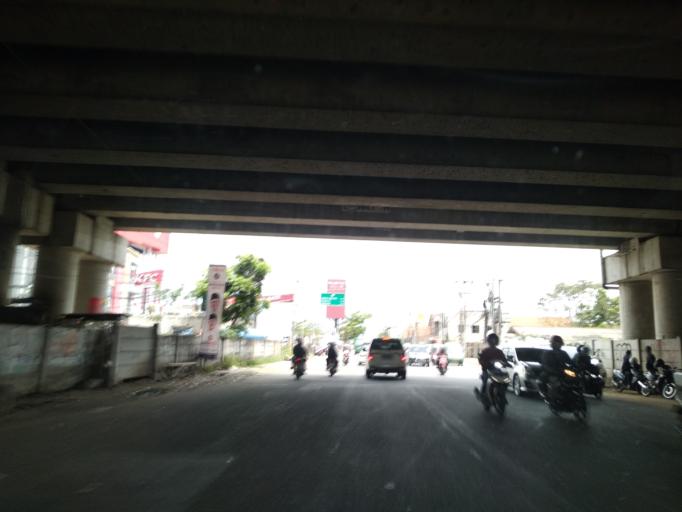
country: ID
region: West Java
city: Pameungpeuk
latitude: -6.9657
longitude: 107.6380
